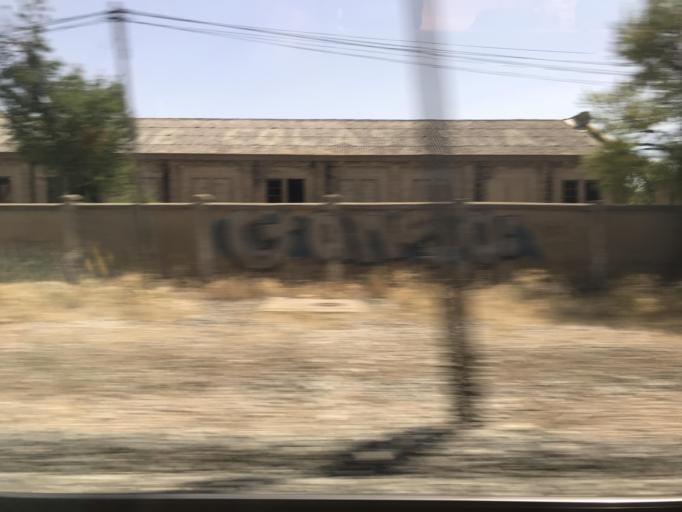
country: ES
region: Castille and Leon
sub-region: Provincia de Valladolid
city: Cabezon
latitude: 41.7395
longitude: -4.6495
